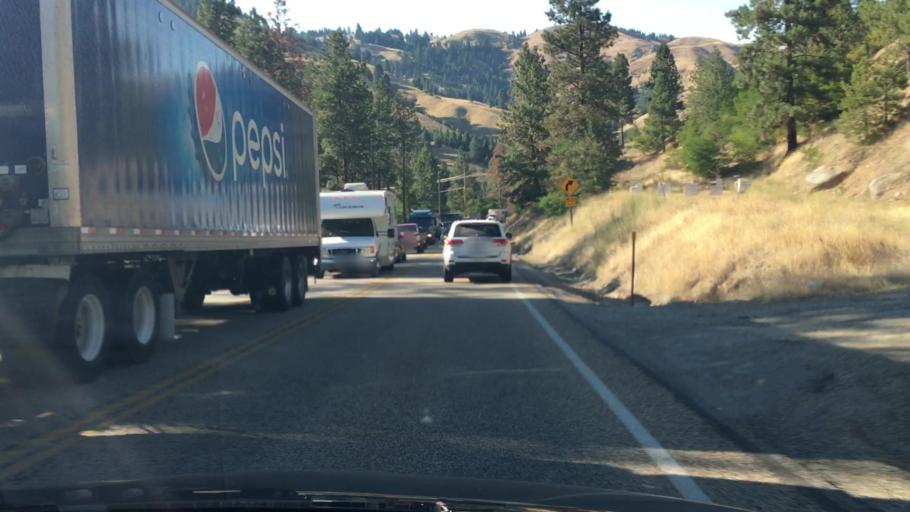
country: US
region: Idaho
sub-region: Boise County
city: Idaho City
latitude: 44.0486
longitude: -116.1320
